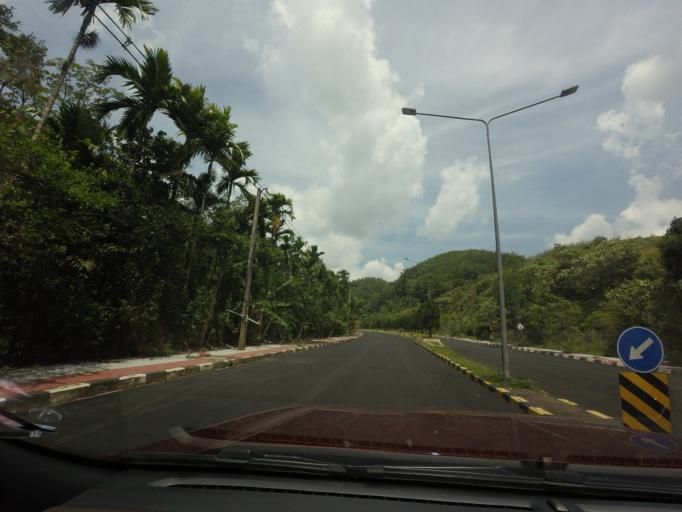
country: TH
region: Yala
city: Betong
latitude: 5.7613
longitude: 101.0465
